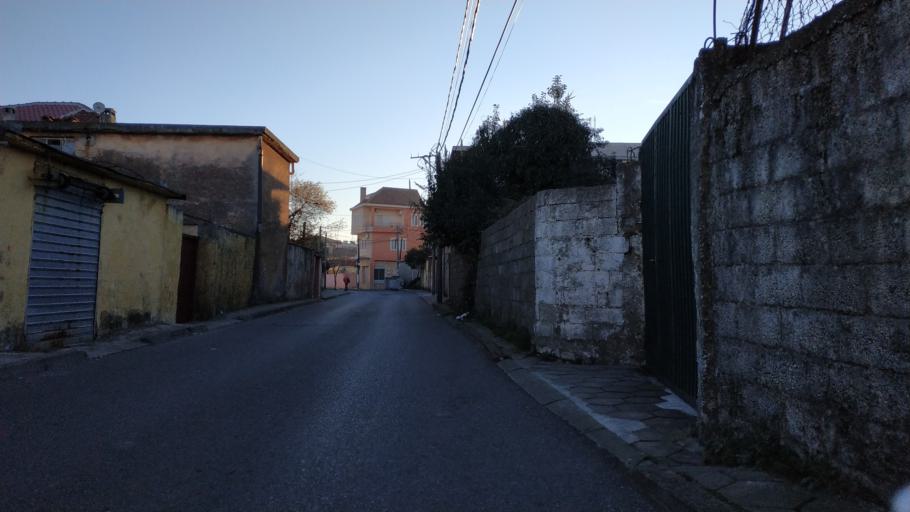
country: AL
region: Shkoder
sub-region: Rrethi i Shkodres
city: Shkoder
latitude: 42.0608
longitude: 19.5164
